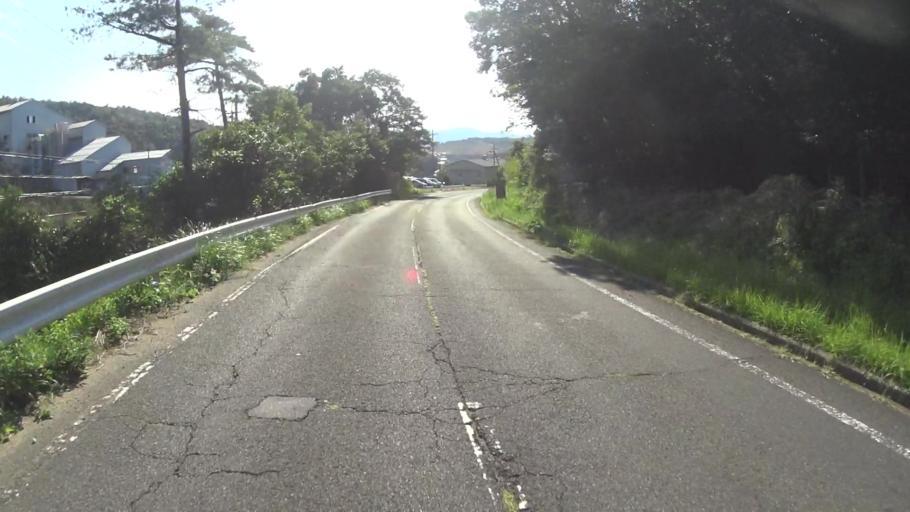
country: JP
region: Kyoto
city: Miyazu
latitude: 35.7018
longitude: 135.0673
